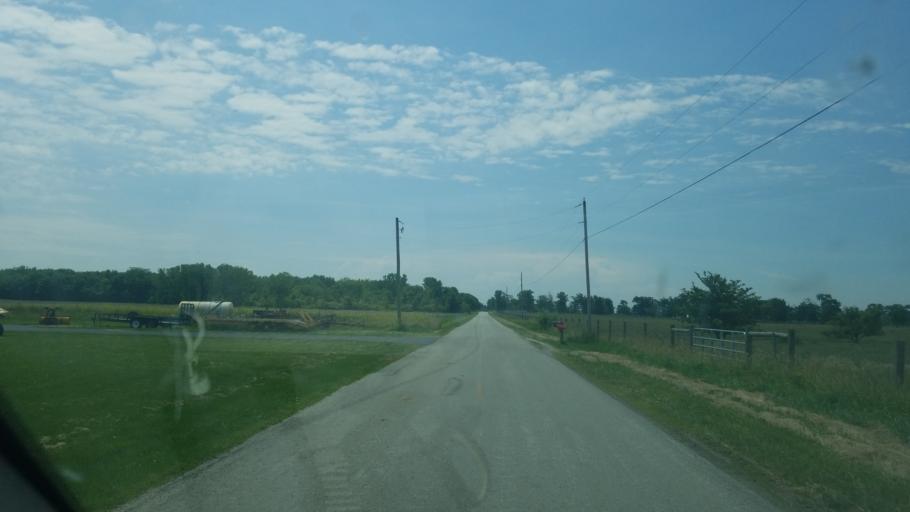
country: US
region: Ohio
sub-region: Wood County
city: North Baltimore
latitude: 41.2387
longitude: -83.6212
